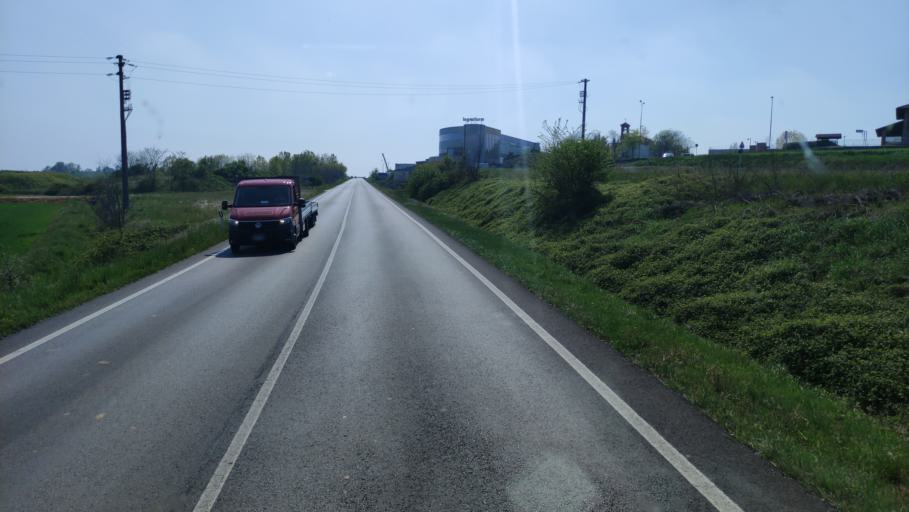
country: IT
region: Piedmont
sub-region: Provincia di Cuneo
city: Marene
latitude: 44.6648
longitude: 7.7512
